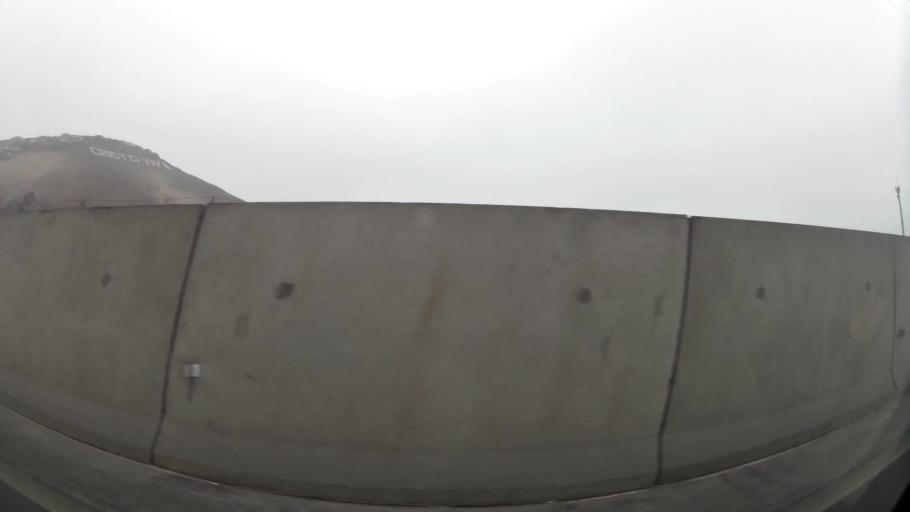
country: PE
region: Lima
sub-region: Lima
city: Santa Rosa
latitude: -11.8159
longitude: -77.1279
